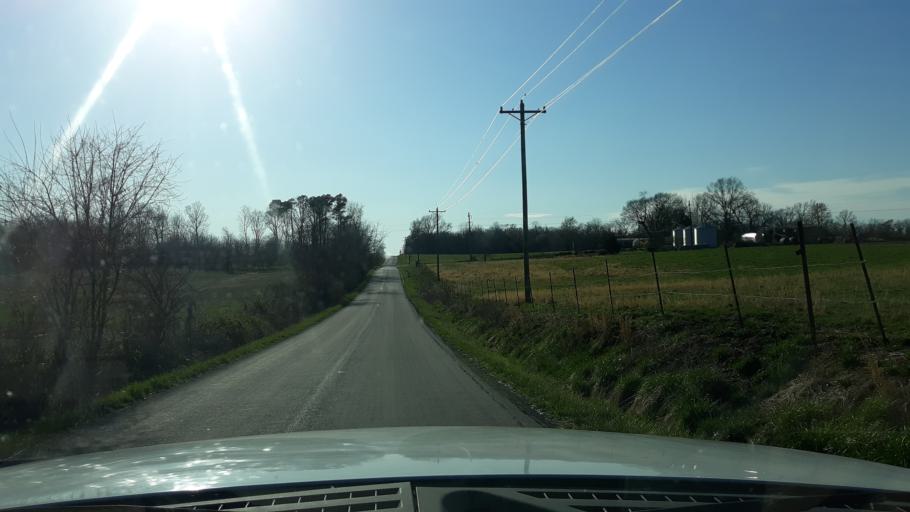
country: US
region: Illinois
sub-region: Saline County
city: Harrisburg
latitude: 37.8047
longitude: -88.6122
